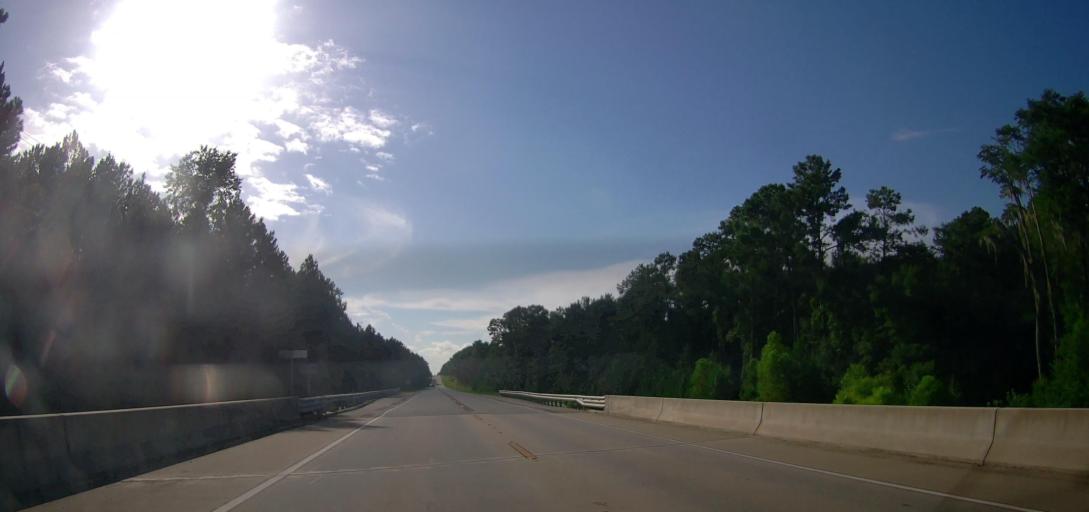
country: US
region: Georgia
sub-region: Coffee County
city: Douglas
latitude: 31.4690
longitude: -82.7673
